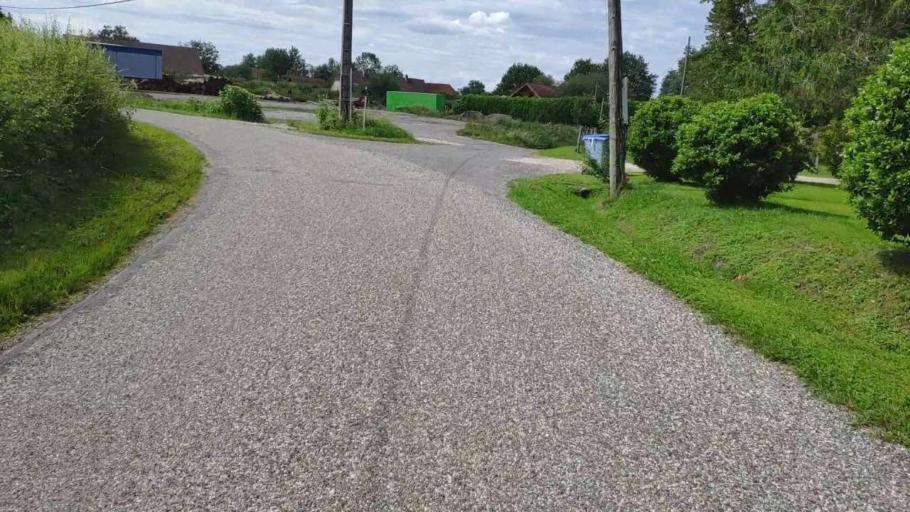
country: FR
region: Franche-Comte
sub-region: Departement du Jura
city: Bletterans
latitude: 46.8203
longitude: 5.4506
